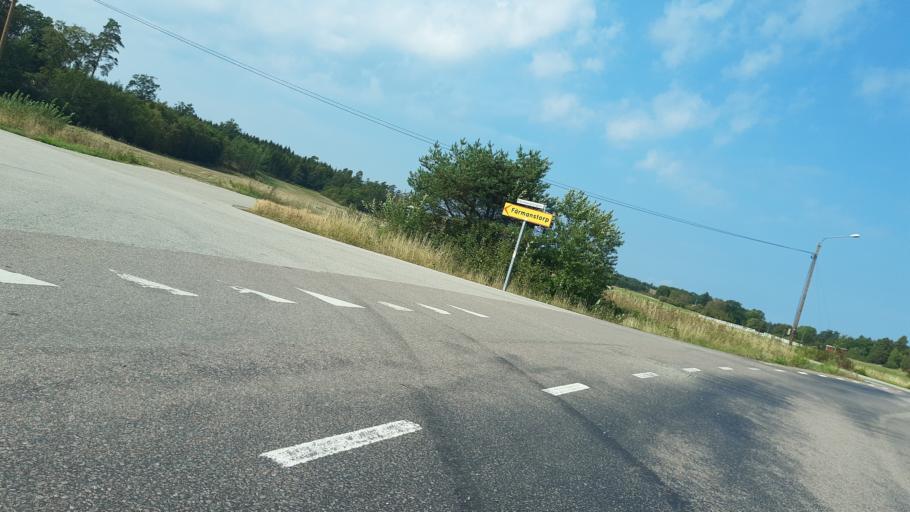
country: SE
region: Blekinge
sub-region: Karlskrona Kommun
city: Nattraby
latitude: 56.1848
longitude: 15.5005
